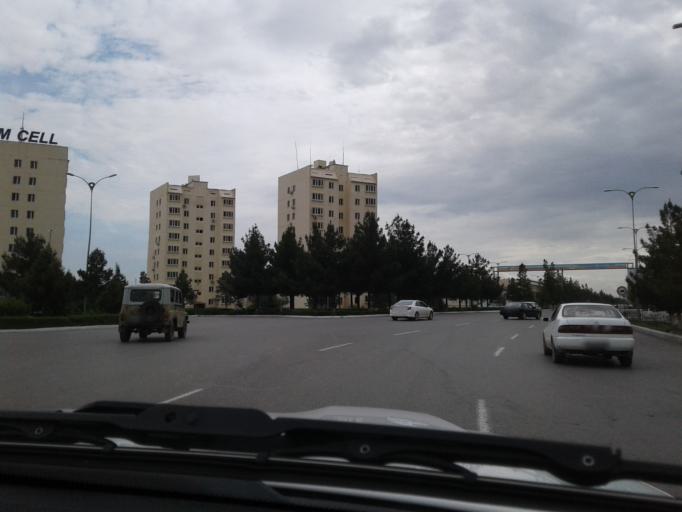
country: TM
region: Mary
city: Mary
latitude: 37.5949
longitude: 61.8767
